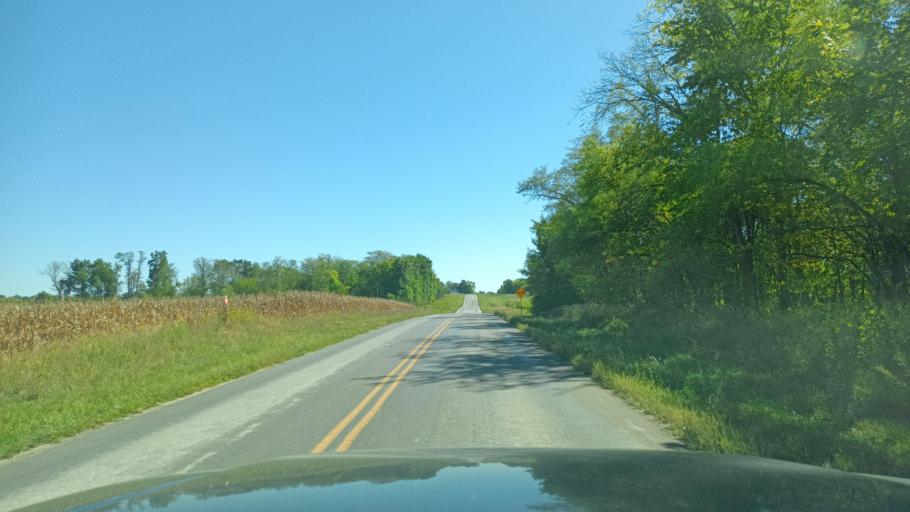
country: US
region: Missouri
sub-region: Macon County
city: La Plata
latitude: 40.0090
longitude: -92.5969
